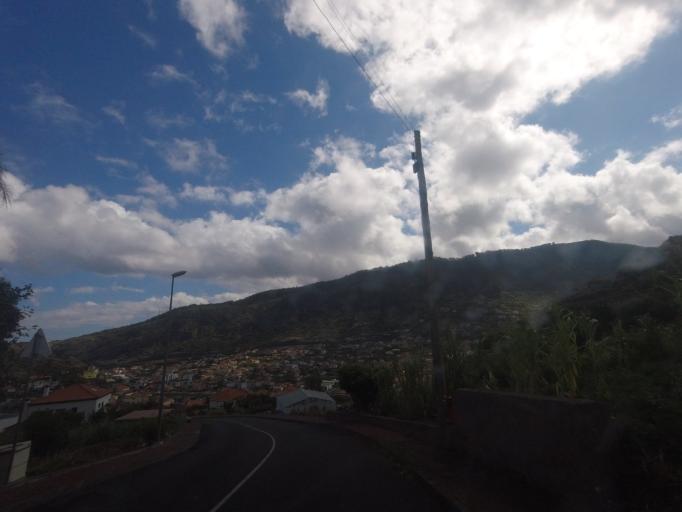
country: PT
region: Madeira
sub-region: Machico
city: Machico
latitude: 32.7296
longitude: -16.7680
